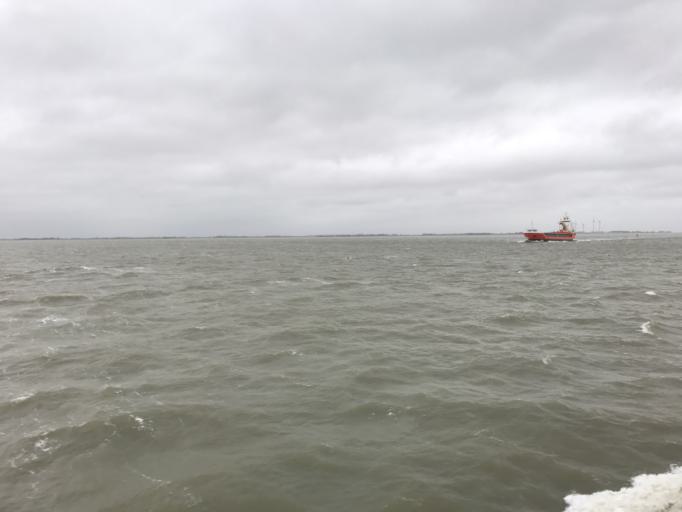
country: NL
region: Groningen
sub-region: Gemeente Delfzijl
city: Delfzijl
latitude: 53.3948
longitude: 6.9537
